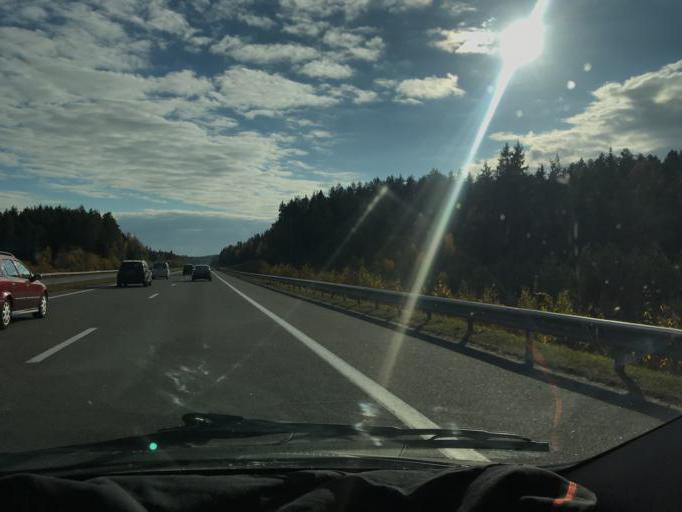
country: BY
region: Minsk
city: Lahoysk
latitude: 54.1391
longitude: 27.8089
